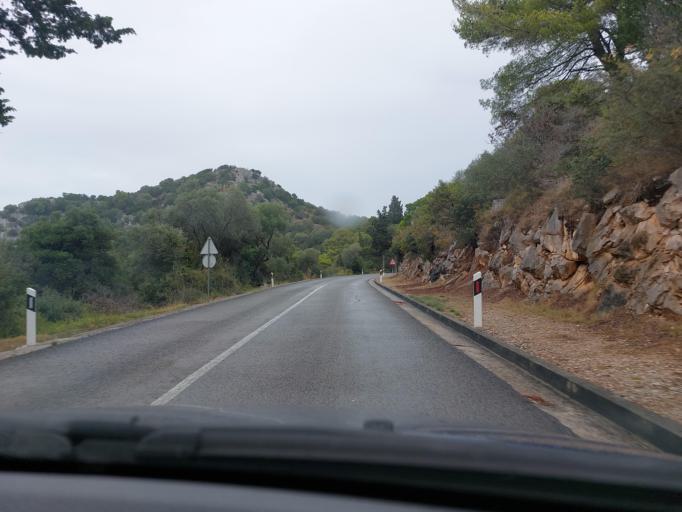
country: HR
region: Dubrovacko-Neretvanska
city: Smokvica
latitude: 42.7701
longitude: 16.8583
